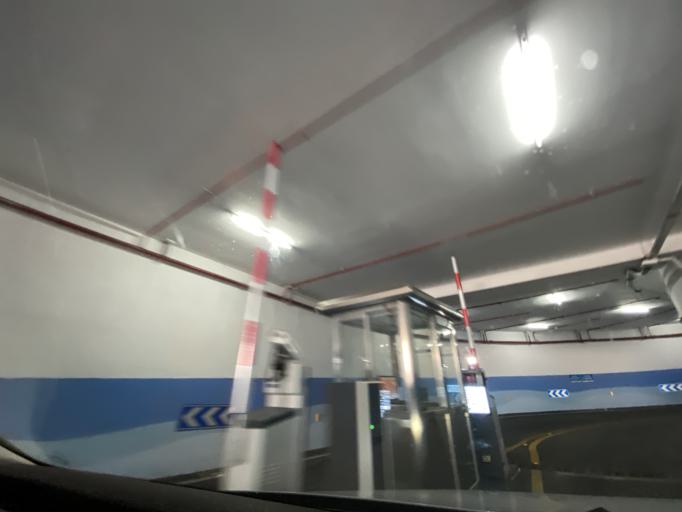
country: CN
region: Hainan
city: Haitangwan
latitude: 18.3771
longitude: 109.7448
